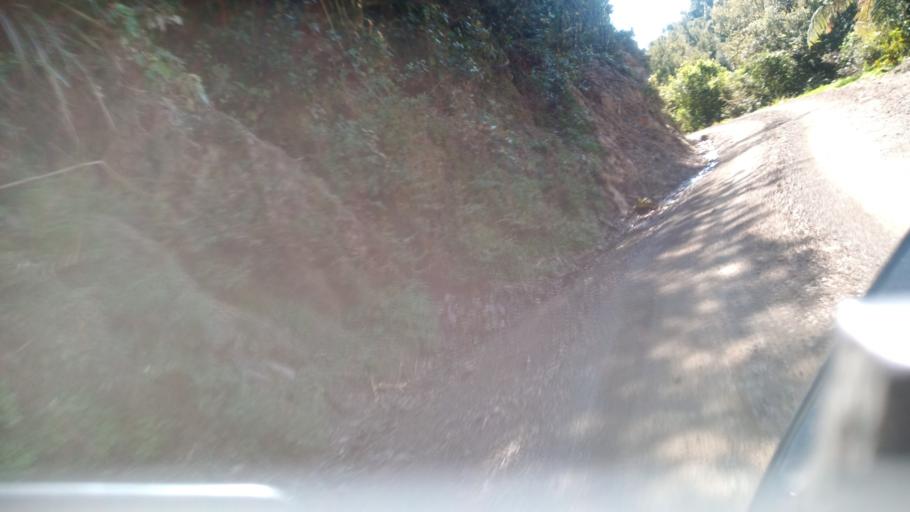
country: NZ
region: Bay of Plenty
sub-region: Opotiki District
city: Opotiki
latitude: -38.0888
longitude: 177.4799
